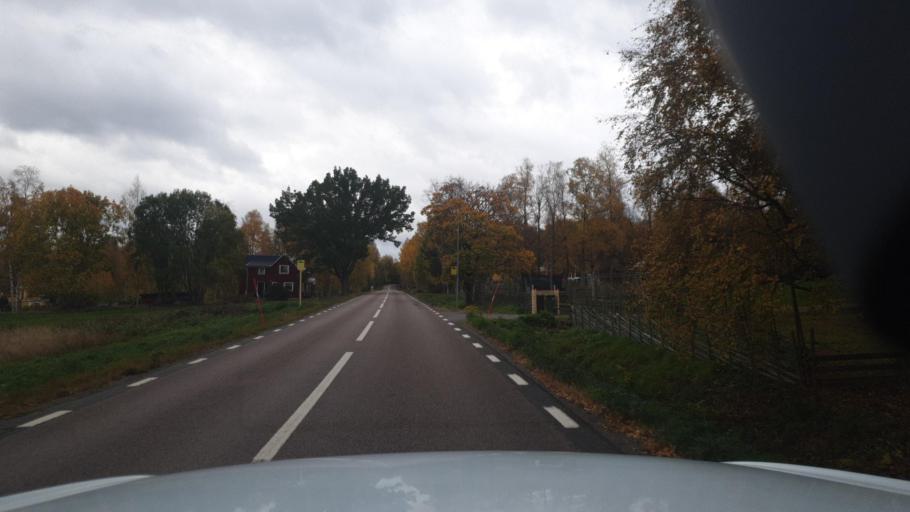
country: SE
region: Vaermland
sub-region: Sunne Kommun
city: Sunne
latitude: 59.8890
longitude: 12.9210
